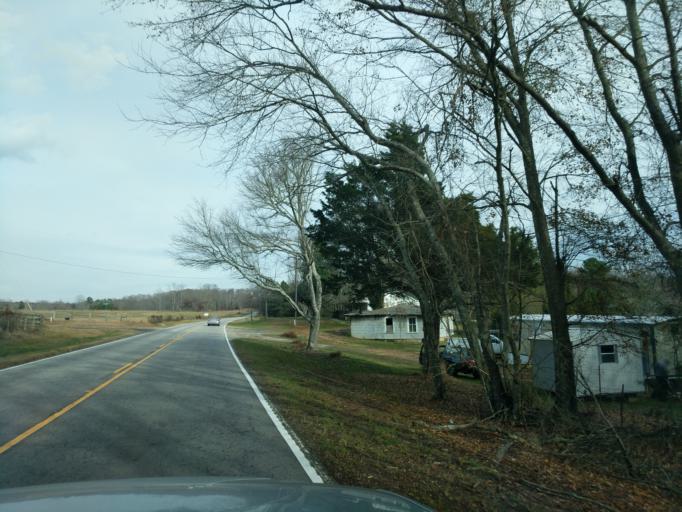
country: US
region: South Carolina
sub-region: Pickens County
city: Central
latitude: 34.6978
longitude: -82.7397
